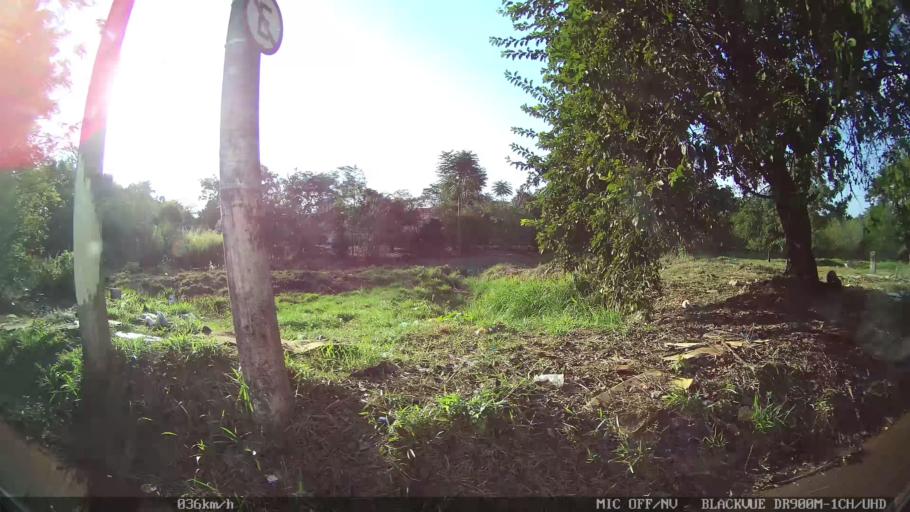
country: BR
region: Sao Paulo
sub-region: Ribeirao Preto
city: Ribeirao Preto
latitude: -21.1460
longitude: -47.8351
